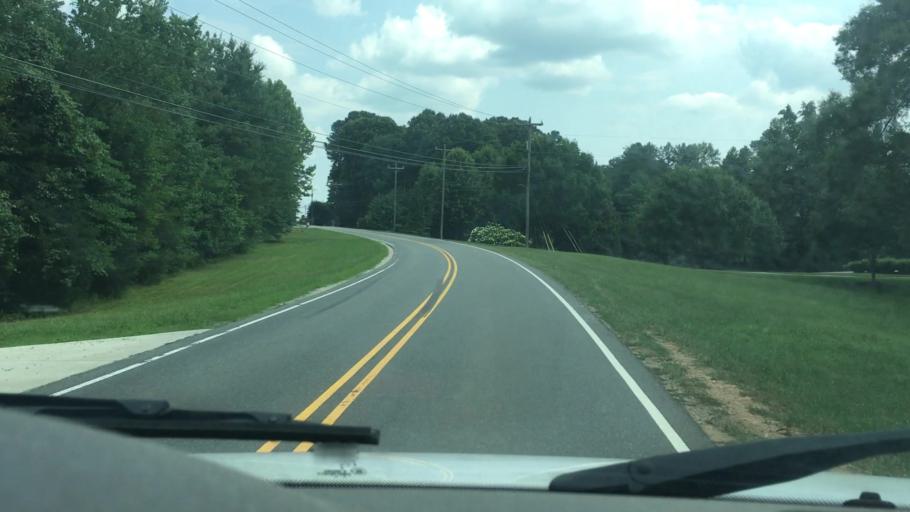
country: US
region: North Carolina
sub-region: Gaston County
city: Davidson
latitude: 35.4705
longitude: -80.8161
